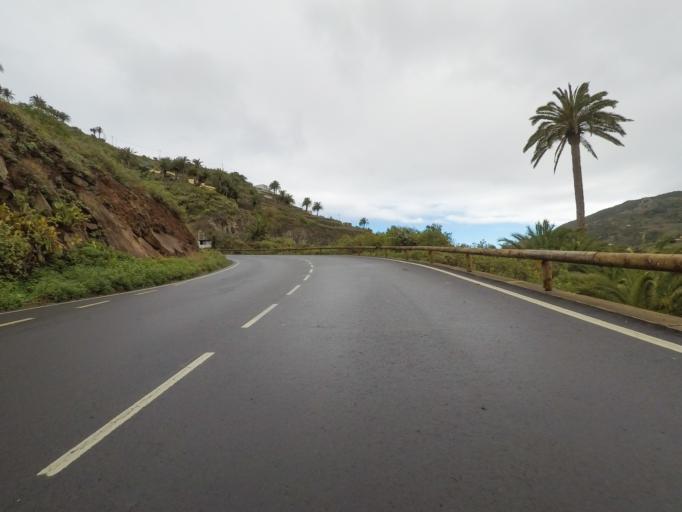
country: ES
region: Canary Islands
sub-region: Provincia de Santa Cruz de Tenerife
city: Agulo
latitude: 28.1844
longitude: -17.2260
